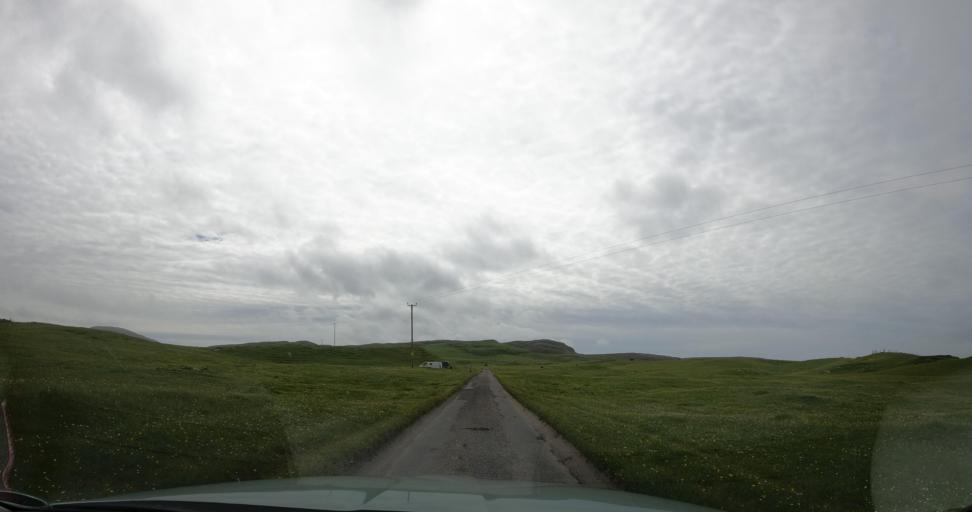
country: GB
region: Scotland
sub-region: Eilean Siar
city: Barra
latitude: 56.9256
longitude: -7.5370
